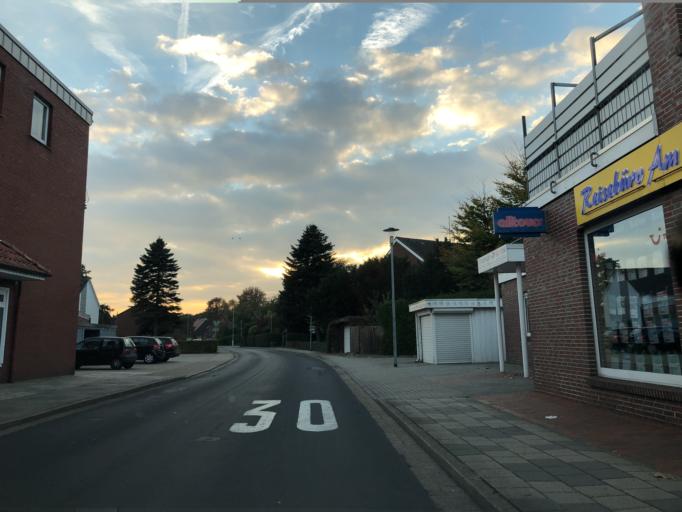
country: DE
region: Lower Saxony
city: Papenburg
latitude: 53.0760
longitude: 7.4396
